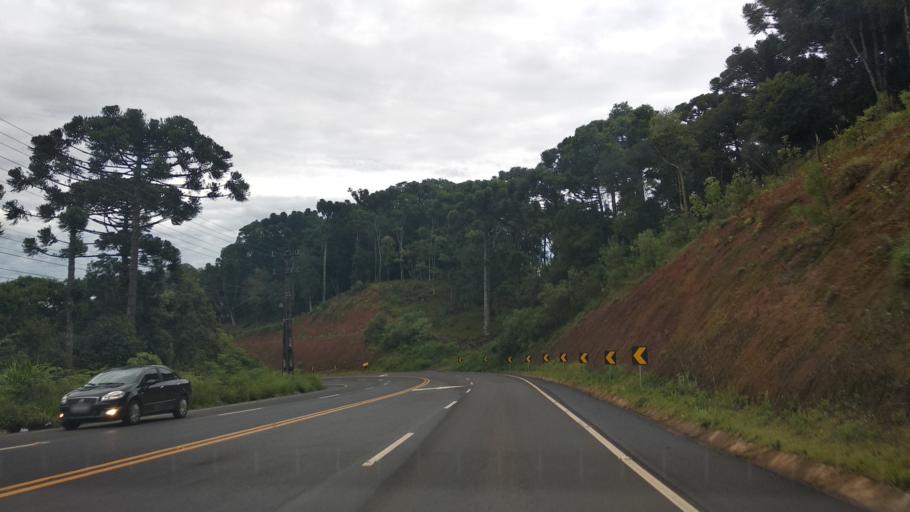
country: BR
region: Santa Catarina
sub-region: Videira
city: Videira
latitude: -27.0520
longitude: -51.1826
